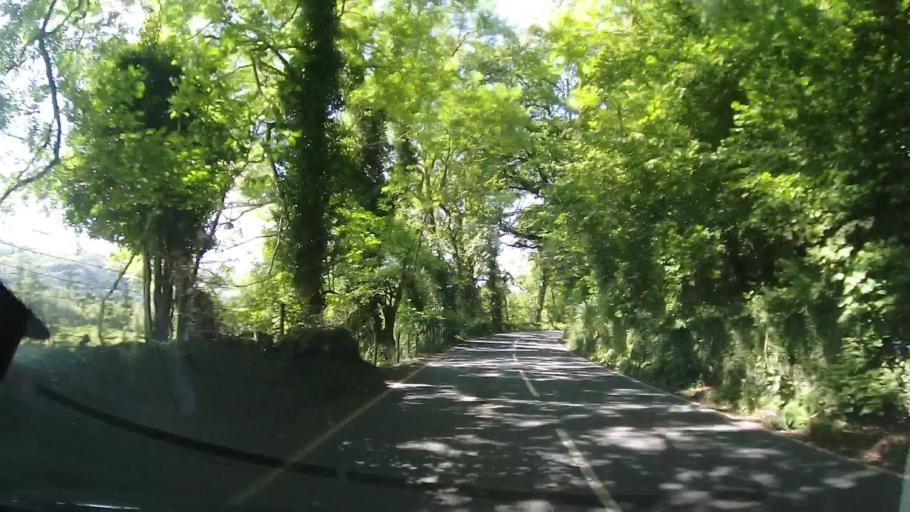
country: GB
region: Wales
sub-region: Sir Powys
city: Machynlleth
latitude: 52.5959
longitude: -3.8693
